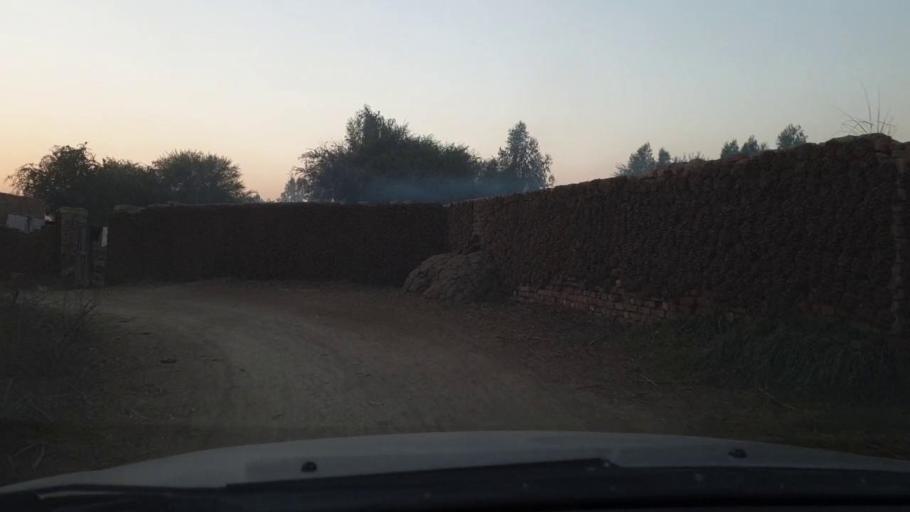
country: PK
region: Sindh
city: Mirpur Mathelo
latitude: 28.0235
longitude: 69.5164
